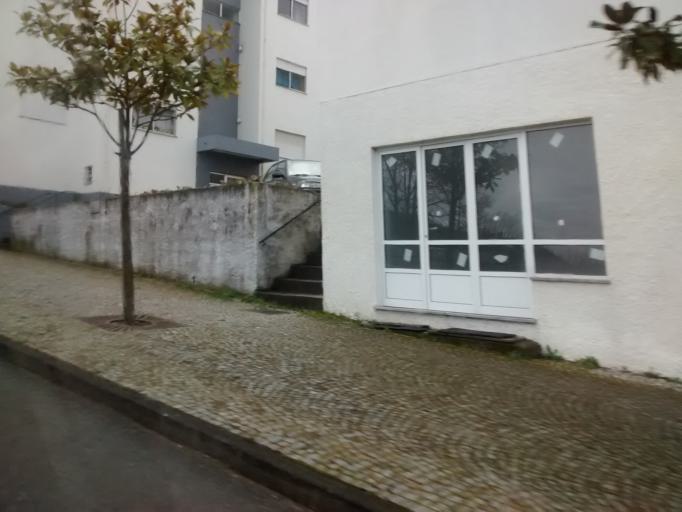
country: PT
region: Guarda
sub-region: Seia
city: Seia
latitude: 40.4131
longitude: -7.7031
